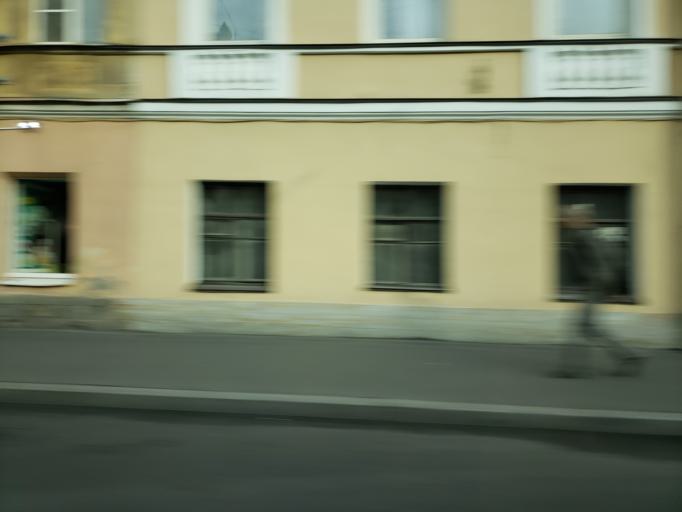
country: RU
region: St.-Petersburg
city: Vasyl'evsky Ostrov
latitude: 59.9473
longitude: 30.2748
